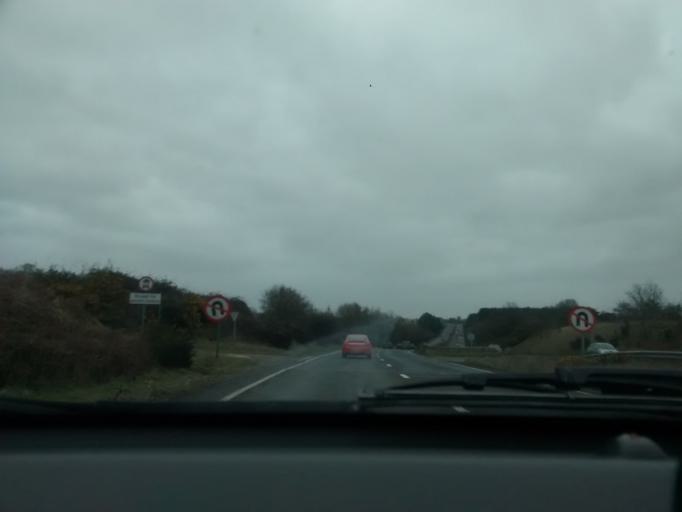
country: GB
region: England
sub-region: Suffolk
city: Kesgrave
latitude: 52.0407
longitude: 1.2632
